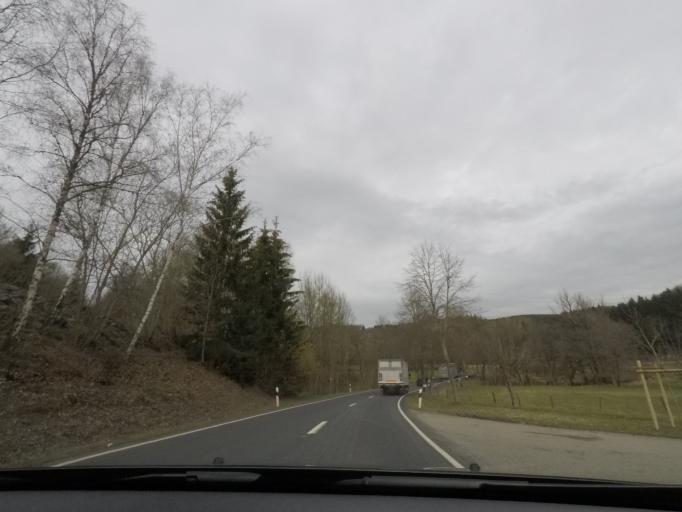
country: LU
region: Diekirch
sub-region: Canton de Wiltz
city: Winseler
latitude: 49.9908
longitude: 5.8560
